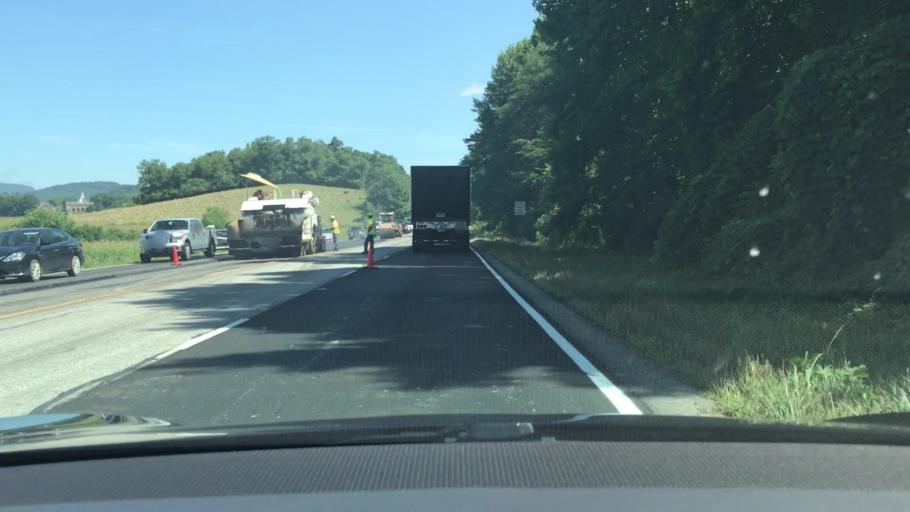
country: US
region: Georgia
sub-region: Rabun County
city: Mountain City
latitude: 34.9505
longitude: -83.3867
